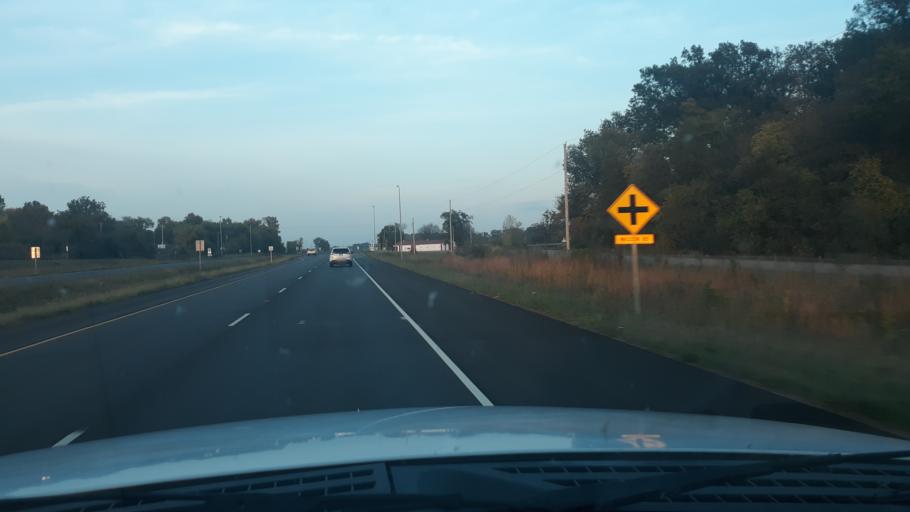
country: US
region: Illinois
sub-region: Saline County
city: Eldorado
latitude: 37.7855
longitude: -88.4876
